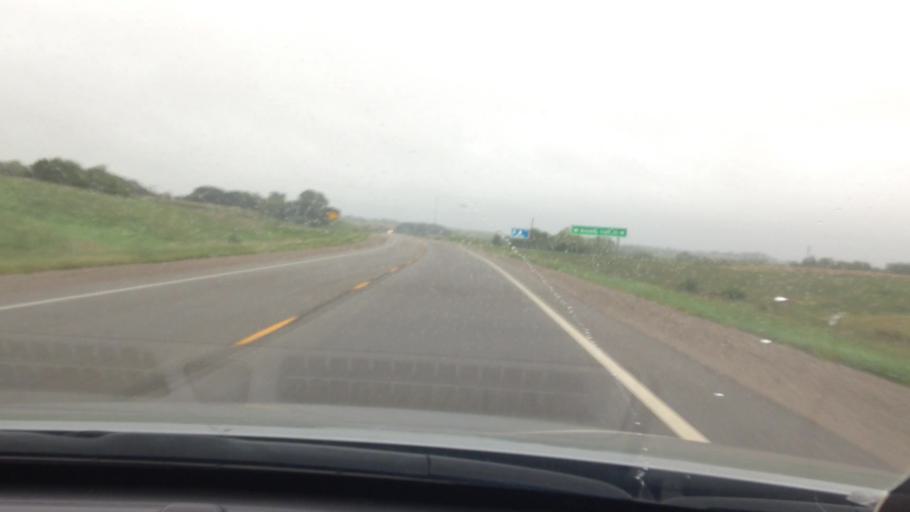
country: US
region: Kansas
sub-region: Doniphan County
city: Troy
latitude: 39.7943
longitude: -95.0845
